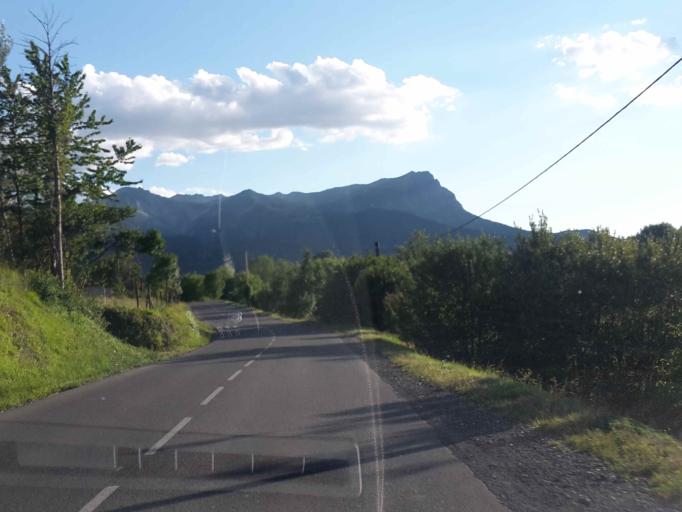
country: FR
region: Provence-Alpes-Cote d'Azur
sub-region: Departement des Hautes-Alpes
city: Embrun
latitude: 44.5511
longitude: 6.5029
